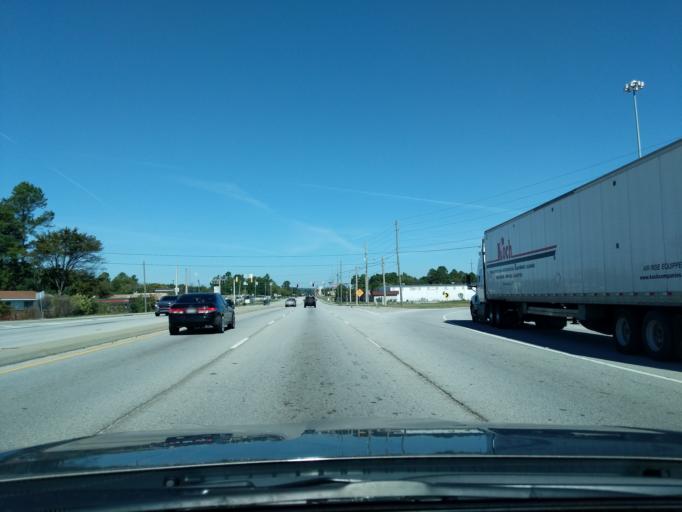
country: US
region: Georgia
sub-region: Richmond County
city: Augusta
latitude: 33.4019
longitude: -82.0058
